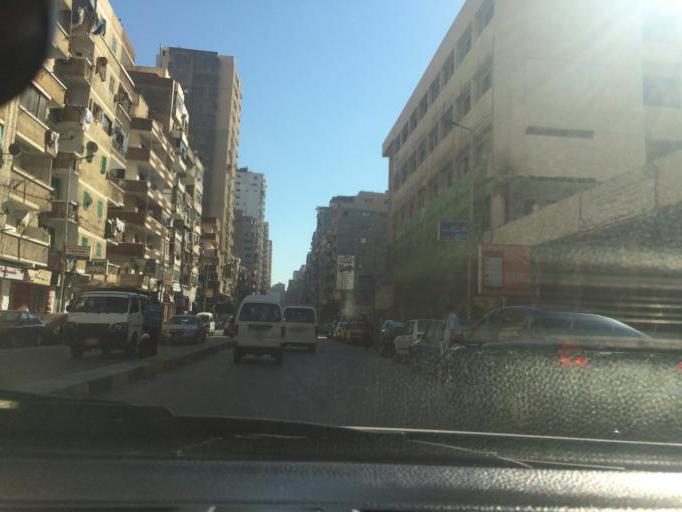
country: EG
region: Alexandria
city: Alexandria
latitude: 31.2618
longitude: 29.9928
